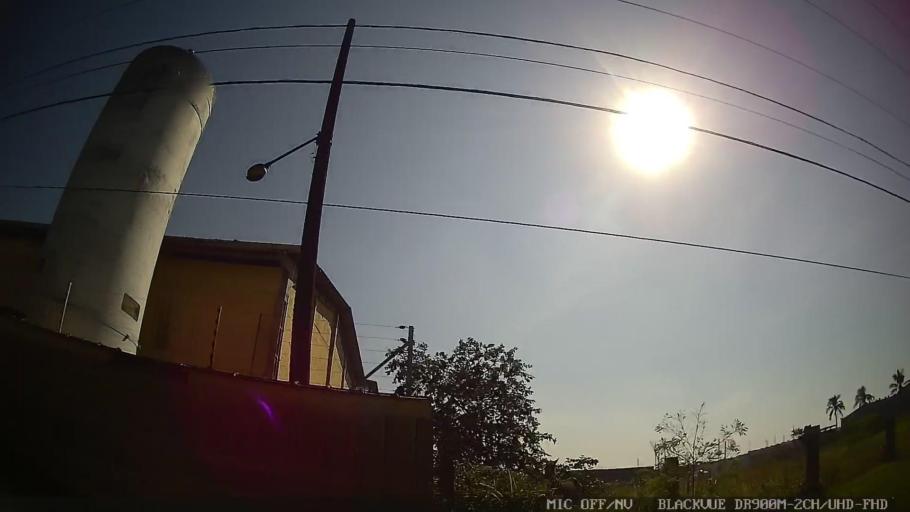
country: BR
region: Sao Paulo
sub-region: Guaruja
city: Guaruja
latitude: -24.0066
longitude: -46.2946
